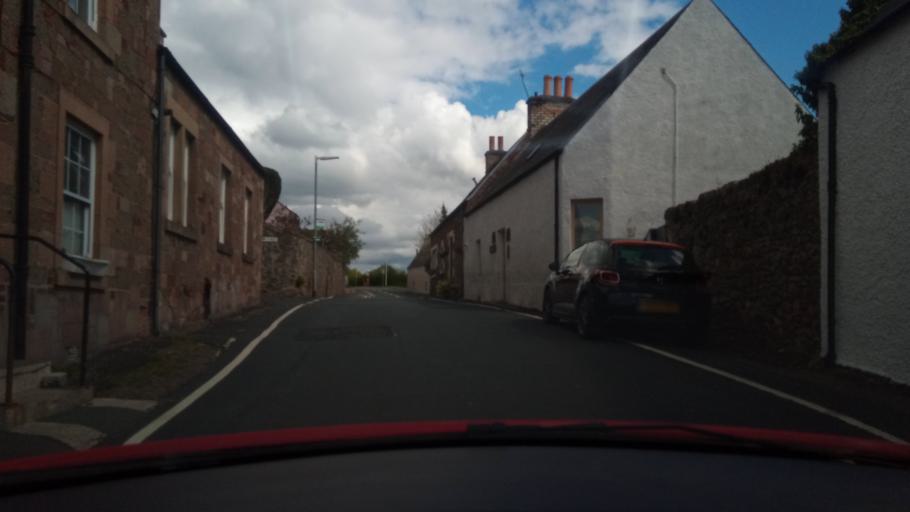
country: GB
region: Scotland
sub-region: The Scottish Borders
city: Newtown St Boswells
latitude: 55.5997
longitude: -2.6943
